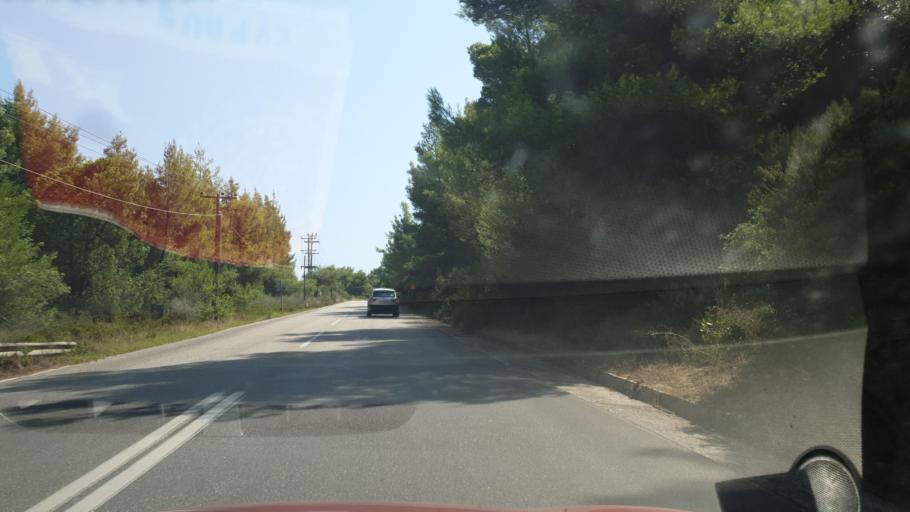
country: GR
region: Central Macedonia
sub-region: Nomos Chalkidikis
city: Sarti
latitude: 40.1130
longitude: 23.9843
